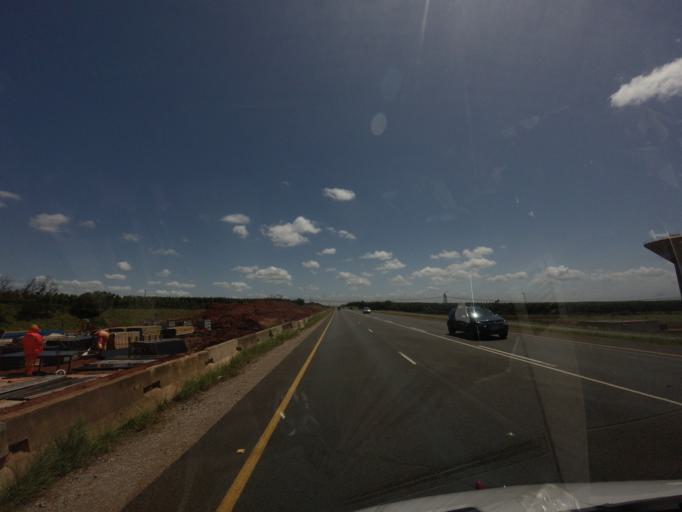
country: ZA
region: KwaZulu-Natal
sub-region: uThungulu District Municipality
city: Empangeni
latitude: -28.7678
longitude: 31.9309
